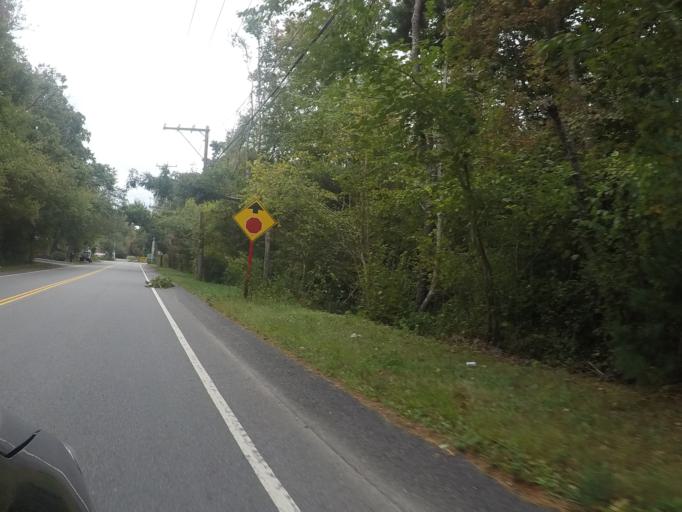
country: US
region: Massachusetts
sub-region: Bristol County
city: Smith Mills
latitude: 41.5855
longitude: -70.9999
